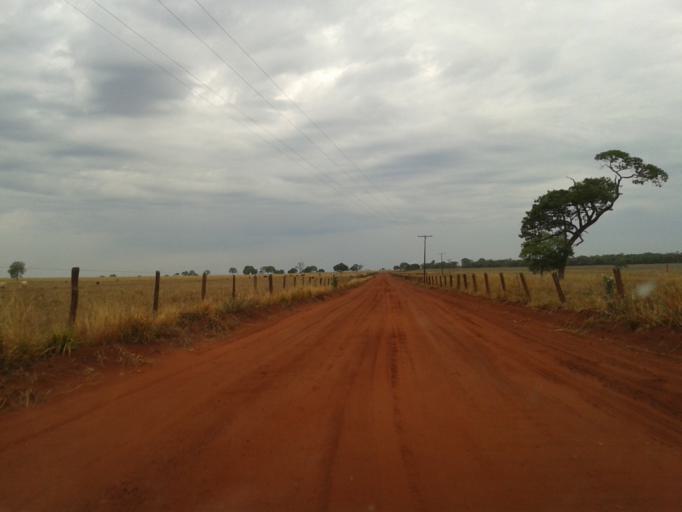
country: BR
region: Minas Gerais
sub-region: Ituiutaba
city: Ituiutaba
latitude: -18.9330
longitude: -49.7374
